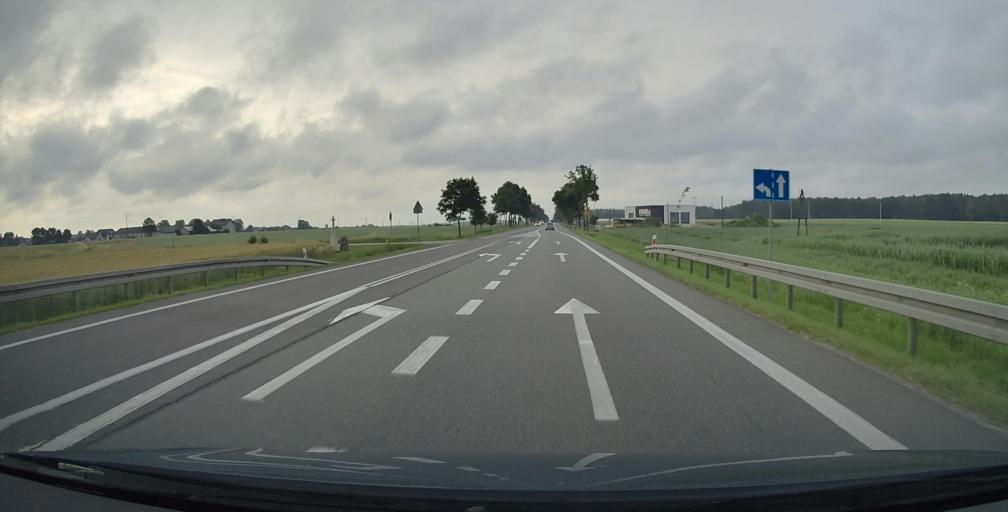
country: PL
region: Masovian Voivodeship
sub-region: Powiat siedlecki
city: Zbuczyn
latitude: 52.1042
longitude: 22.3961
